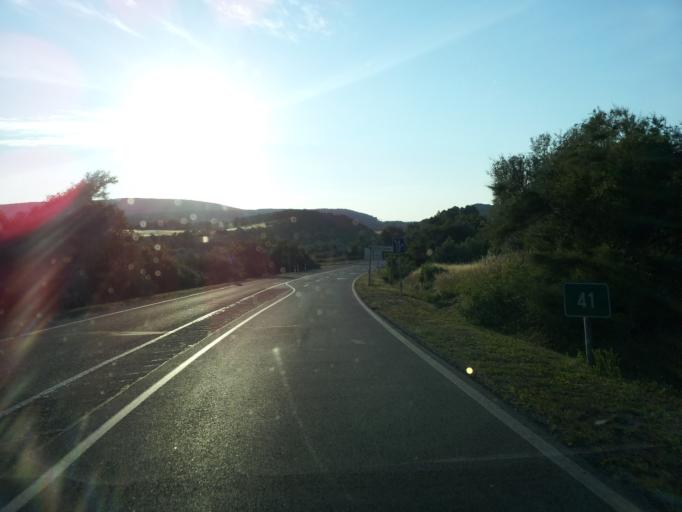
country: HU
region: Fejer
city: Szarliget
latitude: 47.4930
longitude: 18.5140
